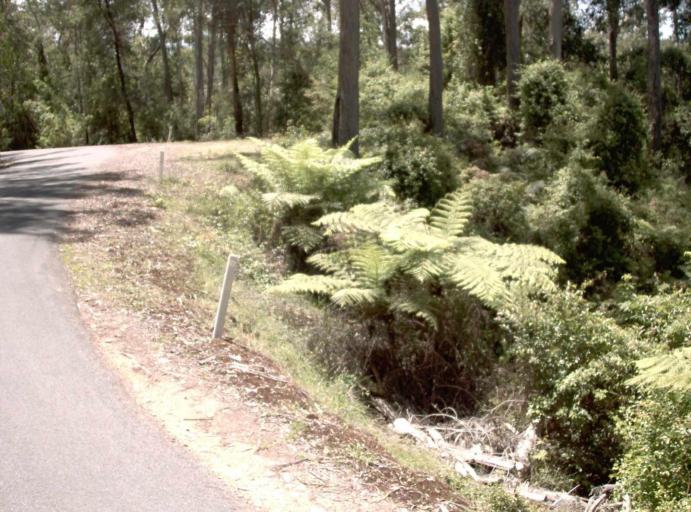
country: AU
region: New South Wales
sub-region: Bombala
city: Bombala
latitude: -37.5012
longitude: 148.9249
